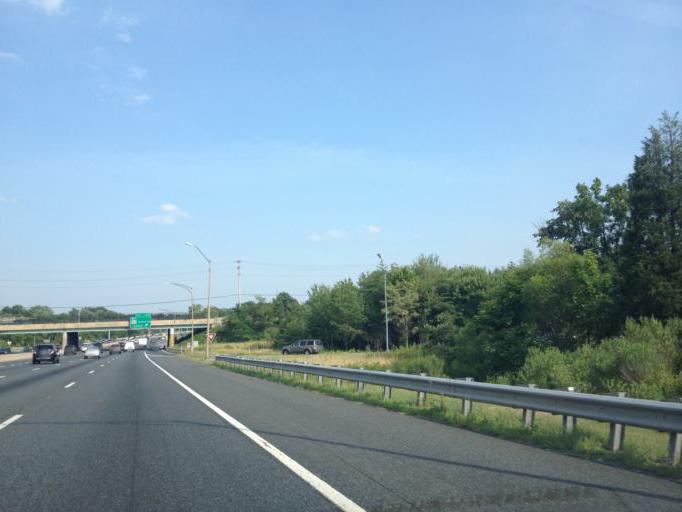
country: US
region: Maryland
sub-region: Baltimore County
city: Carney
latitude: 39.3891
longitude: -76.5325
